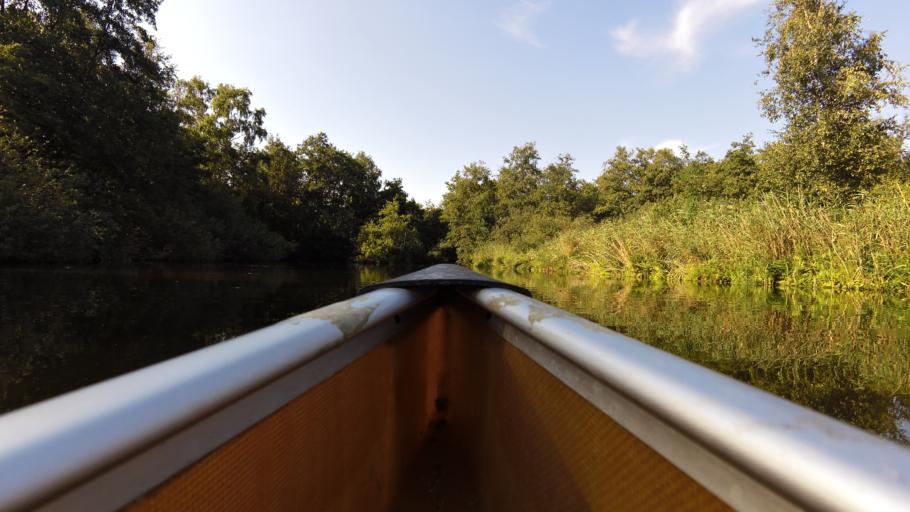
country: NL
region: South Holland
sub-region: Gemeente Nieuwkoop
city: Nieuwkoop
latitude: 52.1315
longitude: 4.7897
